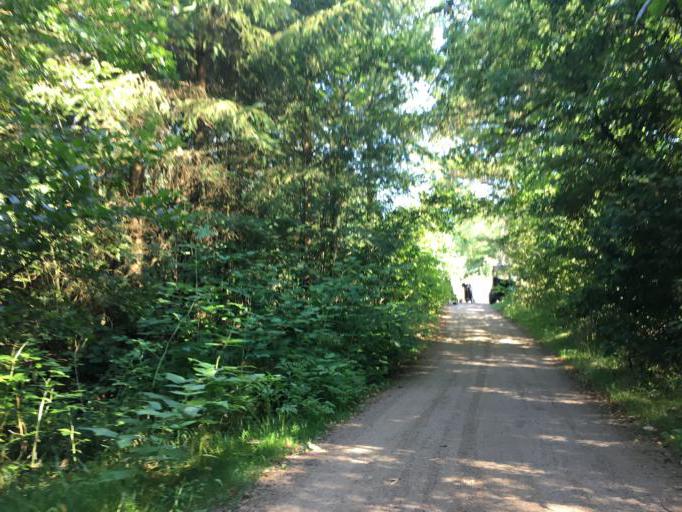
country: DK
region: Central Jutland
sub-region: Holstebro Kommune
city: Ulfborg
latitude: 56.3261
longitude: 8.4131
